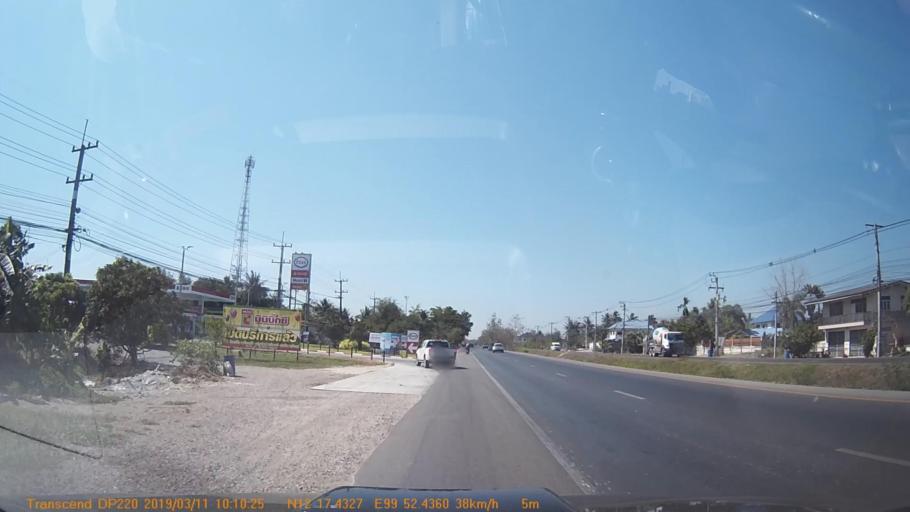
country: TH
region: Prachuap Khiri Khan
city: Sam Roi Yot
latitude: 12.2905
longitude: 99.8740
